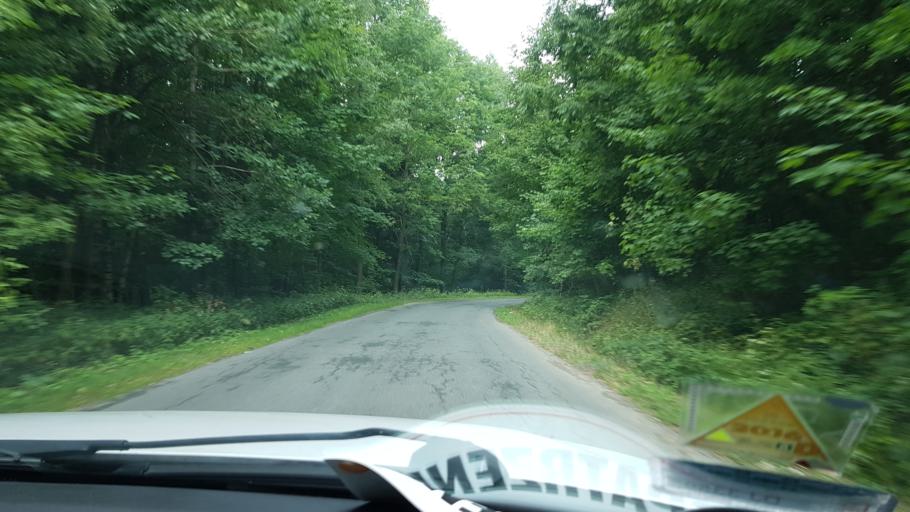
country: PL
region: Lower Silesian Voivodeship
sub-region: Powiat jeleniogorski
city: Jezow Sudecki
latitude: 50.9697
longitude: 15.8206
